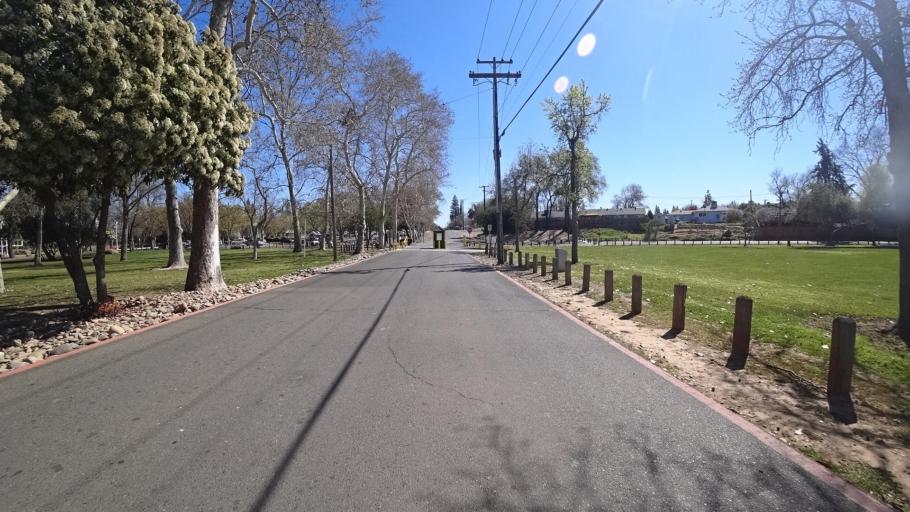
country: US
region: California
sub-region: Sacramento County
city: Rancho Cordova
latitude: 38.6011
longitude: -121.3112
